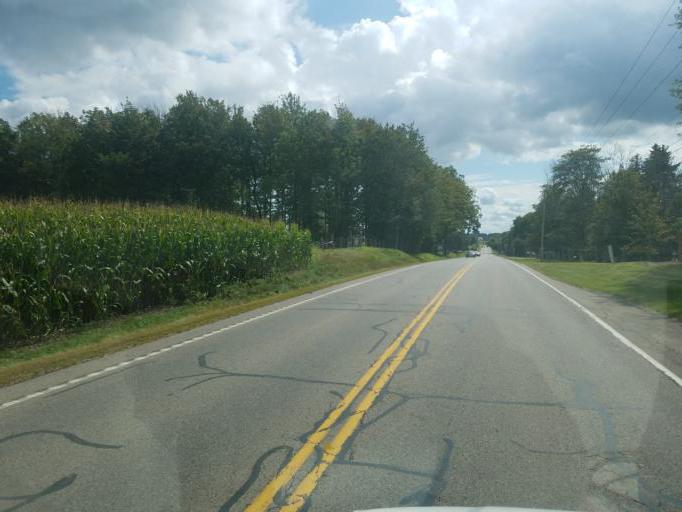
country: US
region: Ohio
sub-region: Richland County
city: Lincoln Heights
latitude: 40.8688
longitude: -82.5134
